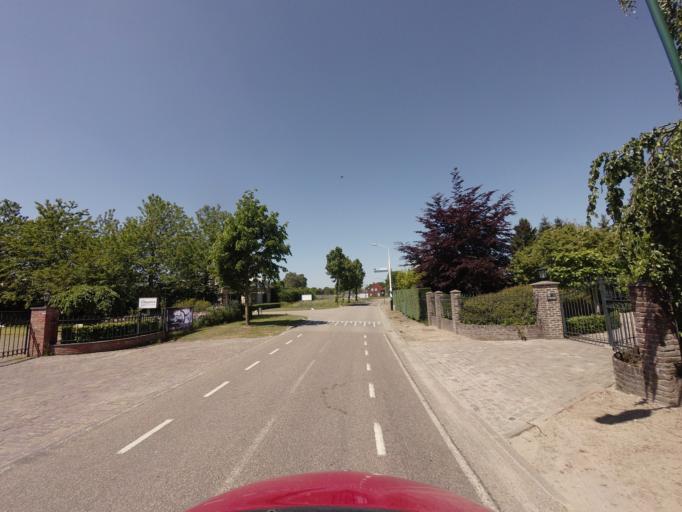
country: NL
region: North Brabant
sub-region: Bergeijk
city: Bergeyk
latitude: 51.2915
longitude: 5.3164
